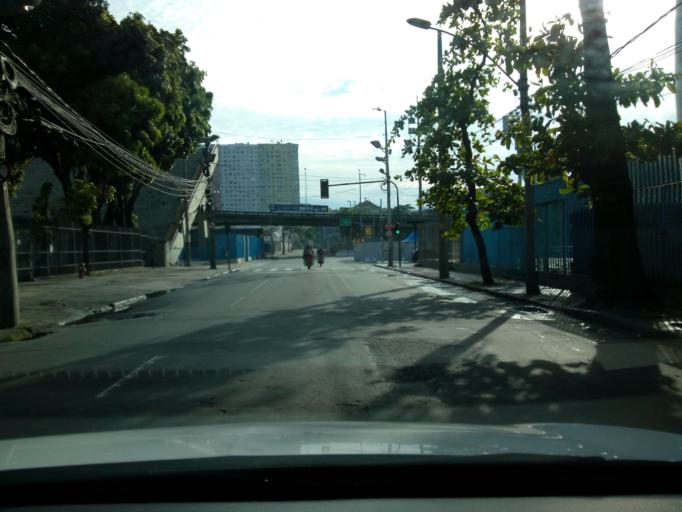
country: BR
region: Rio de Janeiro
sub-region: Rio De Janeiro
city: Rio de Janeiro
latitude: -22.9087
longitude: -43.1983
